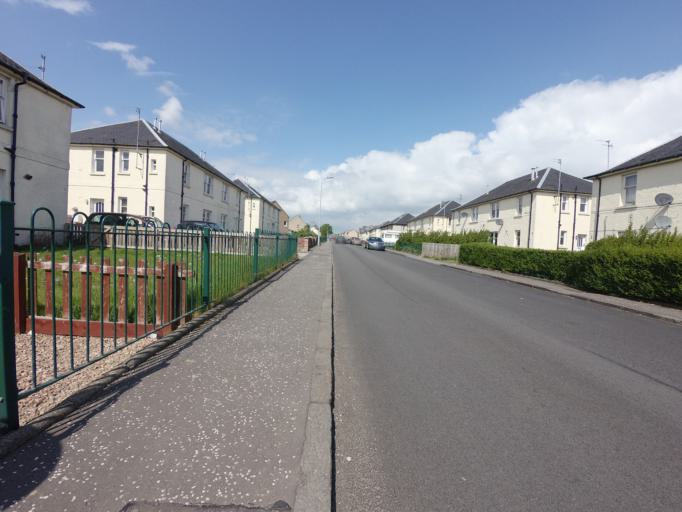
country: GB
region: Scotland
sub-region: Falkirk
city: Falkirk
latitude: 56.0289
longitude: -3.7838
